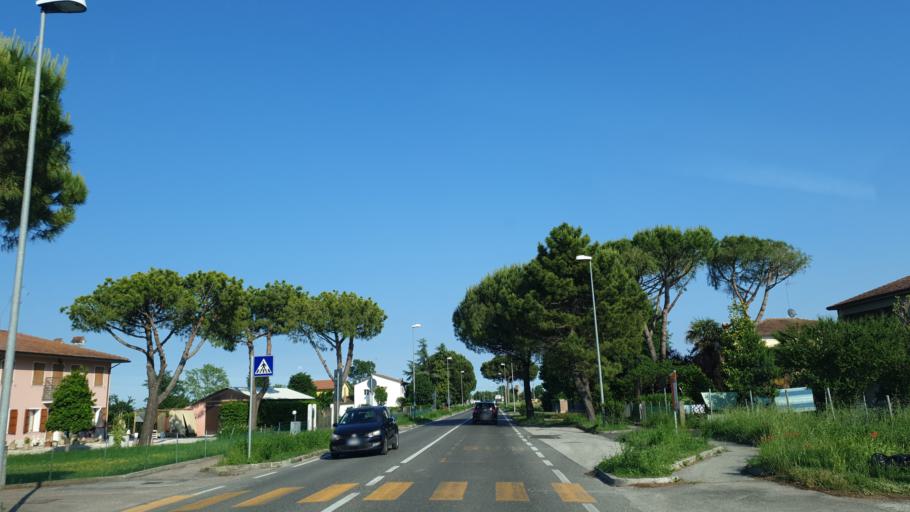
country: IT
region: Emilia-Romagna
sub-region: Provincia di Ravenna
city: Porto Fuori
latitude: 44.4090
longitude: 12.2328
